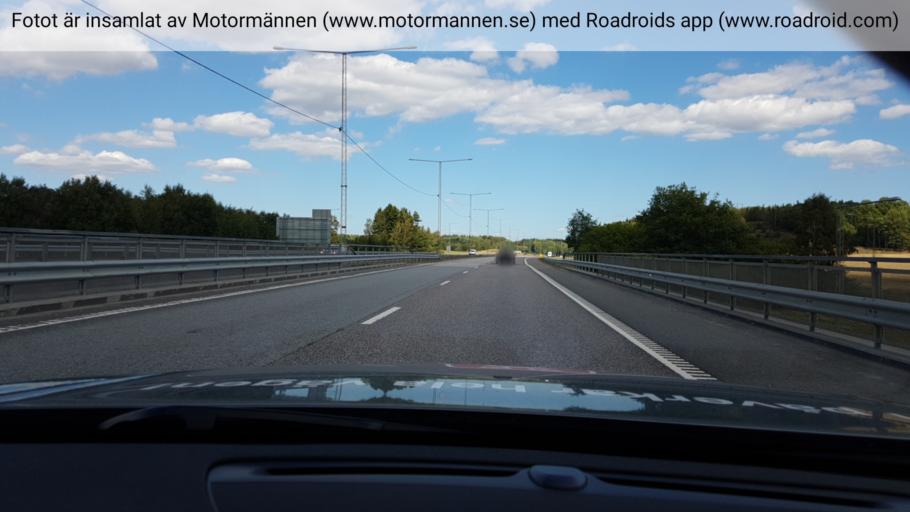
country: SE
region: Stockholm
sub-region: Haninge Kommun
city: Jordbro
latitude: 59.1217
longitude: 18.1323
